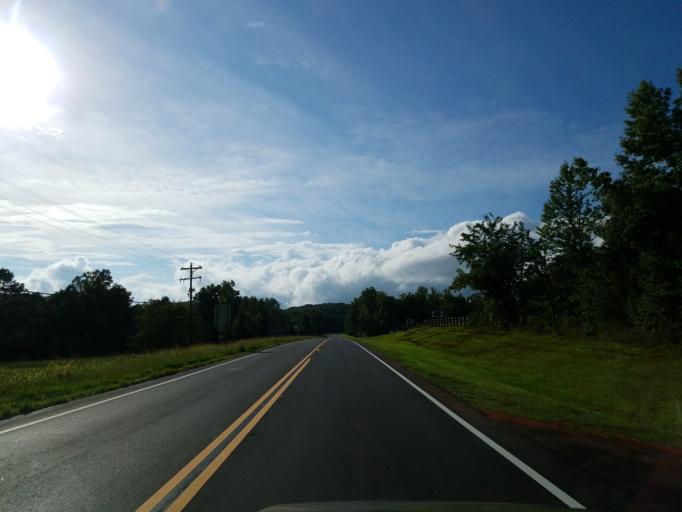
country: US
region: Georgia
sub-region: White County
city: Cleveland
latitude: 34.6361
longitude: -83.8287
